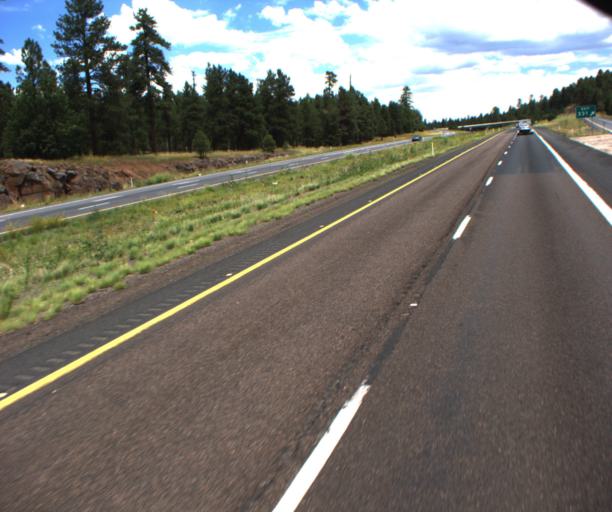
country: US
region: Arizona
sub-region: Coconino County
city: Mountainaire
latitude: 35.0465
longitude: -111.6842
